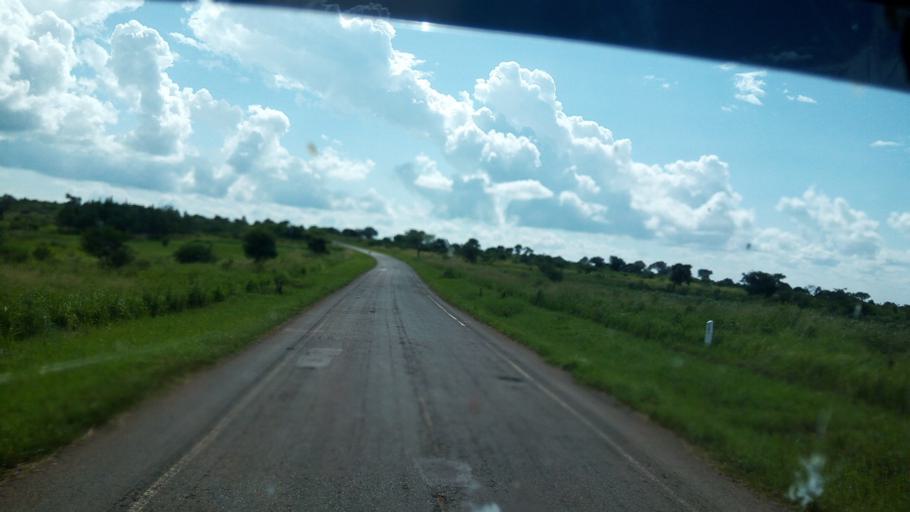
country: UG
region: Northern Region
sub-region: Nwoya District
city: Nwoya
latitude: 2.5391
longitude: 31.8713
